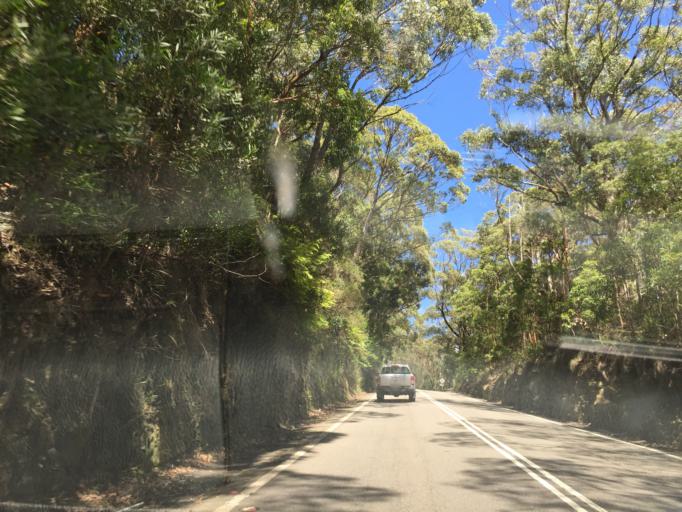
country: AU
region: New South Wales
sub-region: Blue Mountains Municipality
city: Blackheath
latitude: -33.5366
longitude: 150.4215
